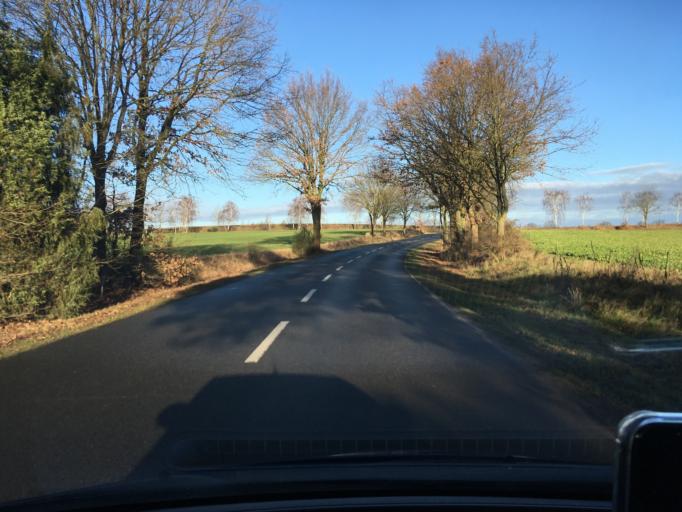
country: DE
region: Lower Saxony
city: Wendisch Evern
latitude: 53.2186
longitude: 10.4774
